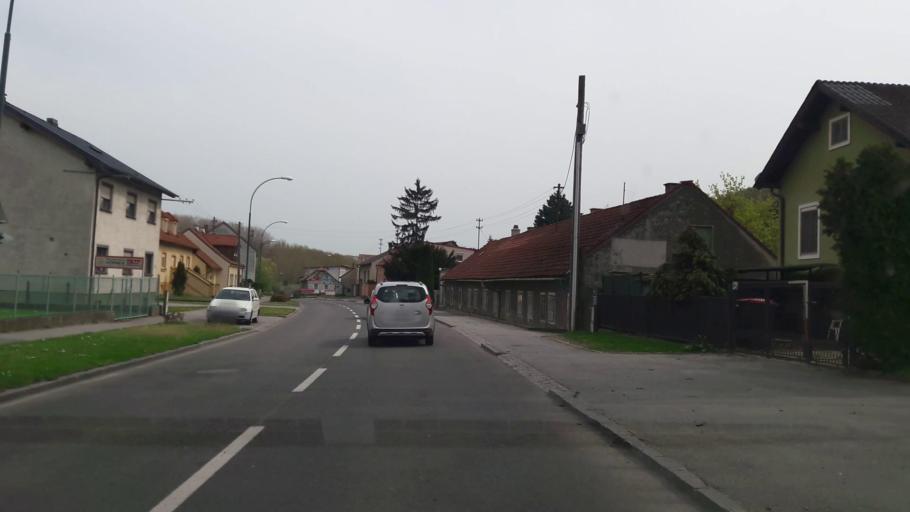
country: AT
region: Lower Austria
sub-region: Politischer Bezirk Bruck an der Leitha
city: Wolfsthal
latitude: 48.1345
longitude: 17.0120
